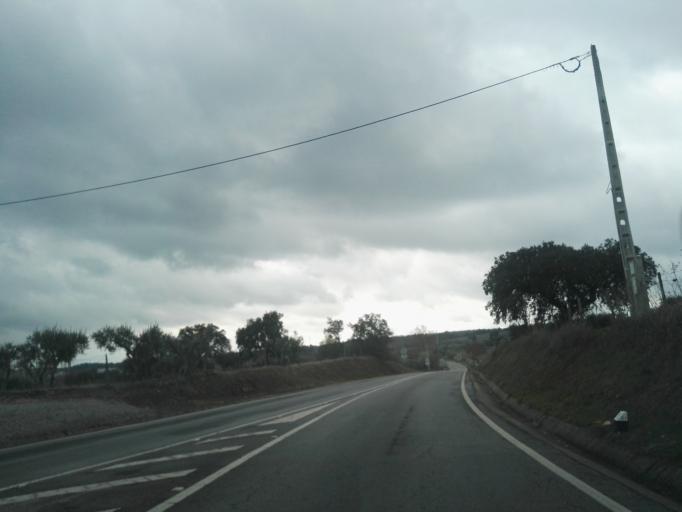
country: PT
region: Portalegre
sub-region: Arronches
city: Arronches
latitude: 39.1236
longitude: -7.2956
